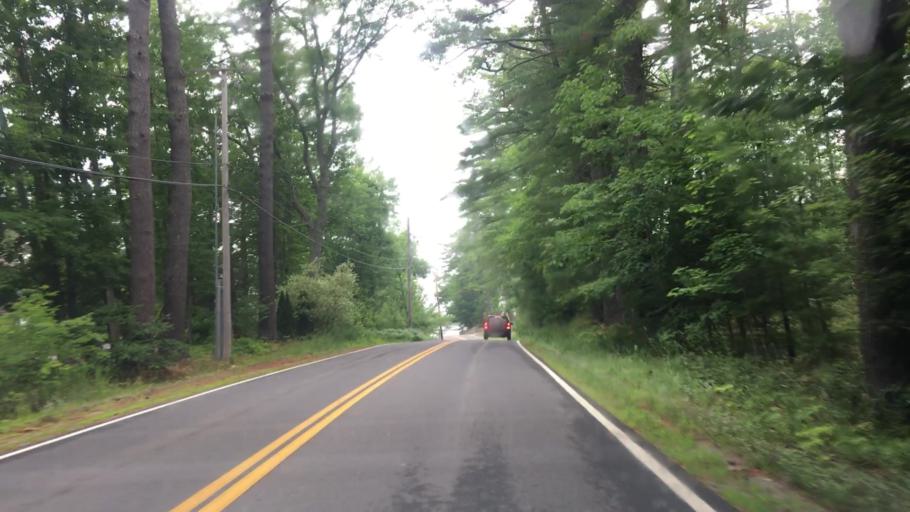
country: US
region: Maine
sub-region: Lincoln County
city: Wiscasset
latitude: 43.9972
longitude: -69.6513
